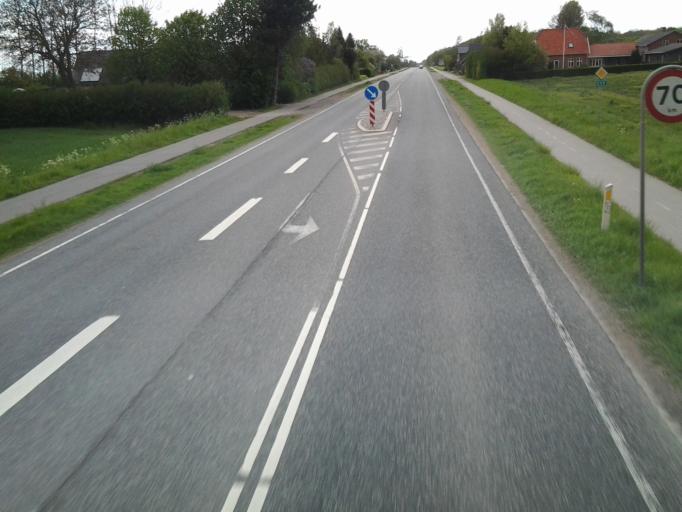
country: DK
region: Zealand
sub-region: Guldborgsund Kommune
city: Nykobing Falster
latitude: 54.8145
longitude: 11.8697
